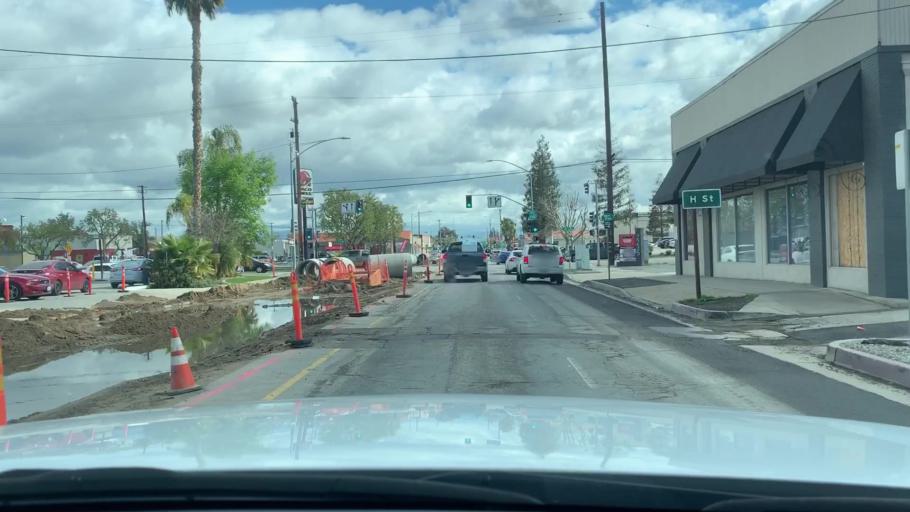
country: US
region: California
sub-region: Kern County
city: Bakersfield
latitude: 35.3801
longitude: -119.0219
